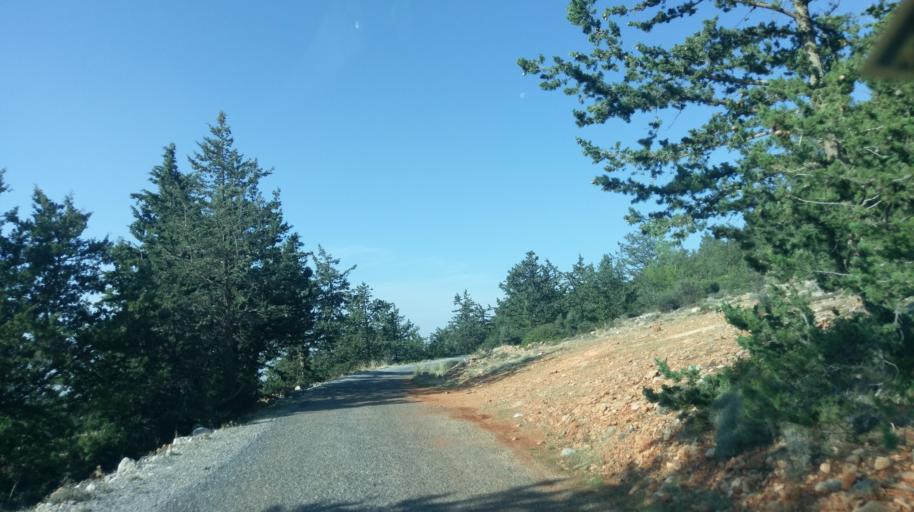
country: CY
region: Lefkosia
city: Nicosia
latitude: 35.2771
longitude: 33.4281
